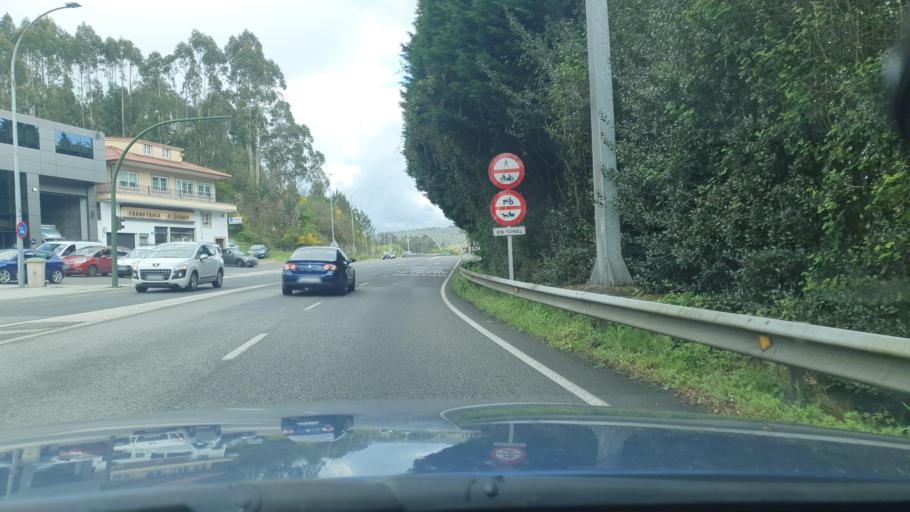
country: ES
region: Galicia
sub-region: Provincia da Coruna
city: Santiago de Compostela
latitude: 42.8719
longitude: -8.5794
